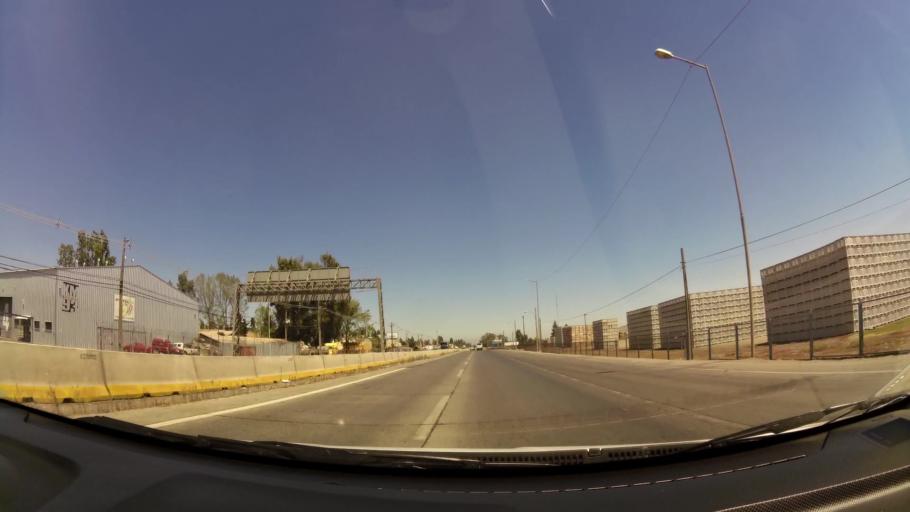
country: CL
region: O'Higgins
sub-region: Provincia de Cachapoal
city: Rancagua
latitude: -34.2126
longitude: -70.7702
